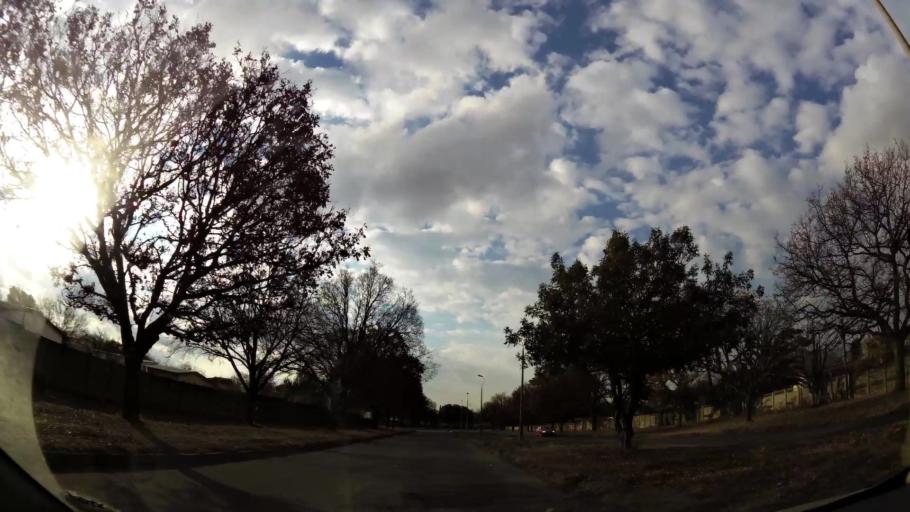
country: ZA
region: Orange Free State
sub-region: Fezile Dabi District Municipality
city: Sasolburg
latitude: -26.8156
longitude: 27.8194
